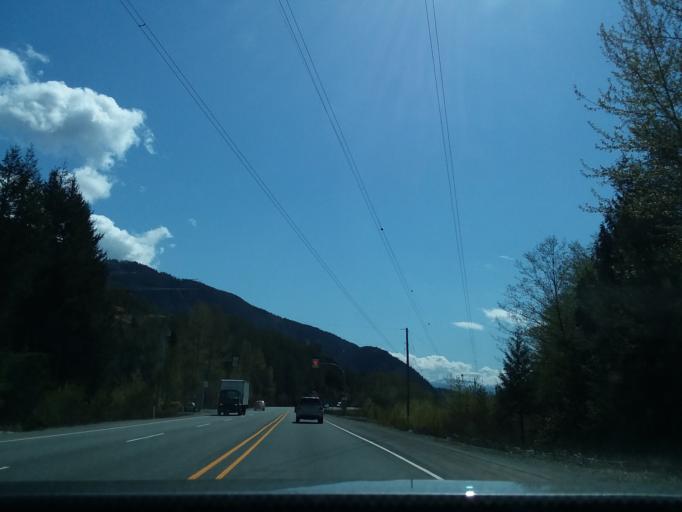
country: CA
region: British Columbia
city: Whistler
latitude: 49.8932
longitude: -123.1612
